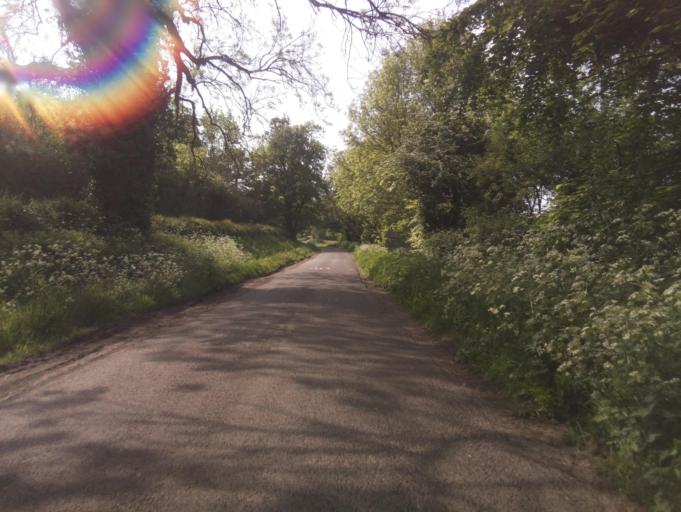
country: GB
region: England
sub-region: Wiltshire
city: Malmesbury
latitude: 51.5483
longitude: -2.1003
